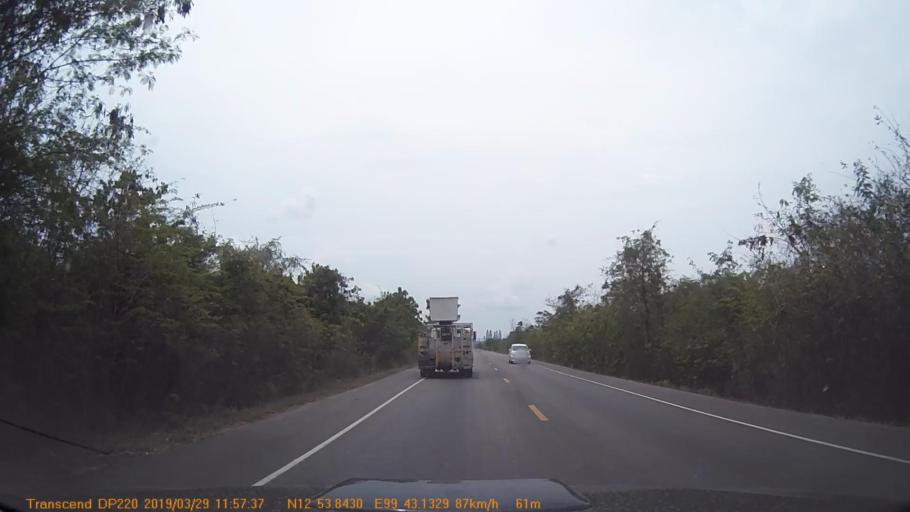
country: TH
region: Phetchaburi
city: Kaeng Krachan
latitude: 12.8969
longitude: 99.7187
